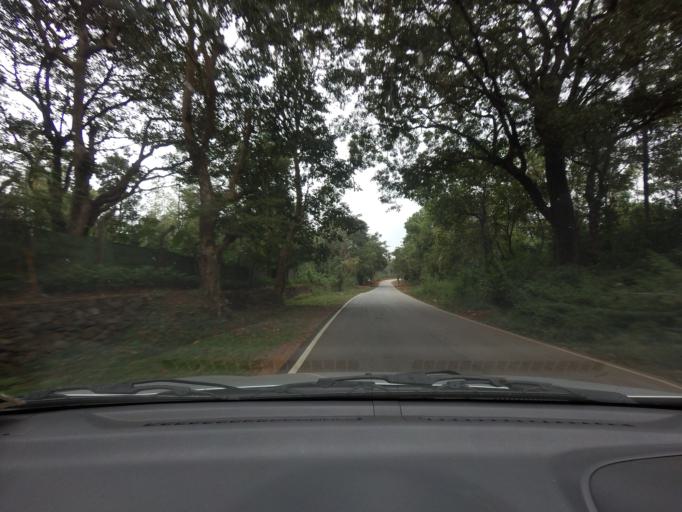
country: IN
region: Karnataka
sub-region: Hassan
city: Sakleshpur
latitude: 12.9384
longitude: 75.7577
